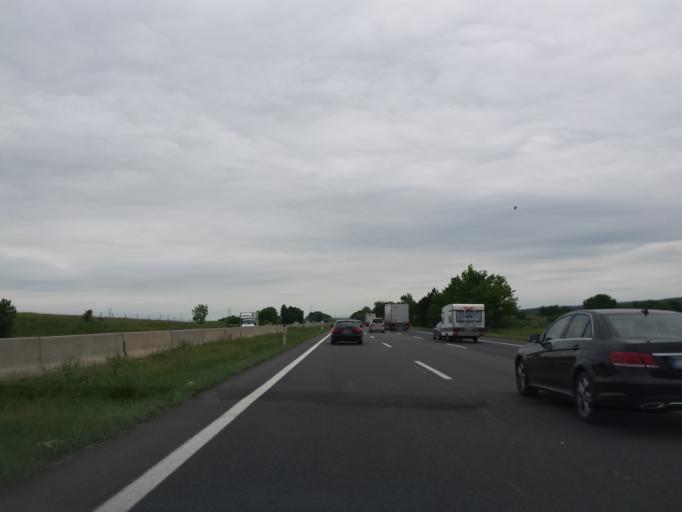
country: AT
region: Lower Austria
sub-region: Politischer Bezirk Baden
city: Leobersdorf
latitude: 47.9151
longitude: 16.2082
